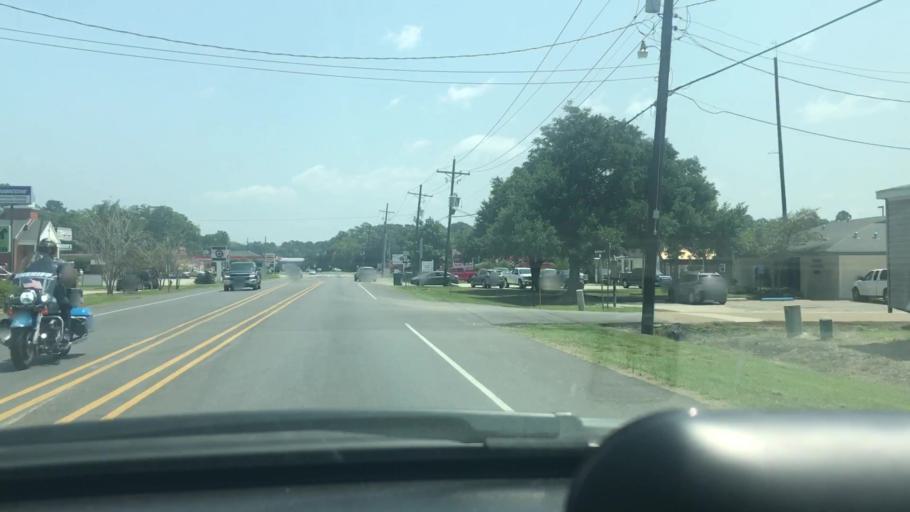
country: US
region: Louisiana
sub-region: Livingston Parish
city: Walker
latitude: 30.4879
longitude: -90.8640
